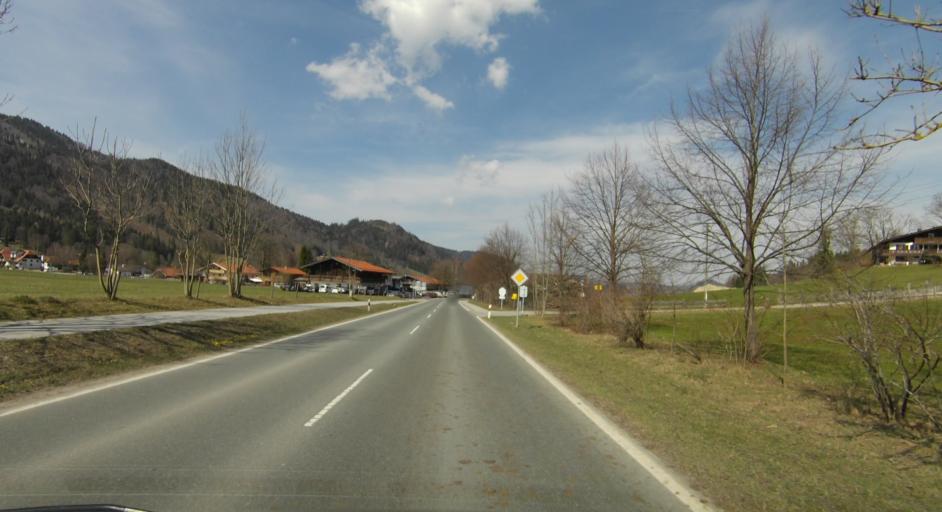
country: DE
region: Bavaria
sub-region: Upper Bavaria
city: Schliersee
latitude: 47.7105
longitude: 11.8715
